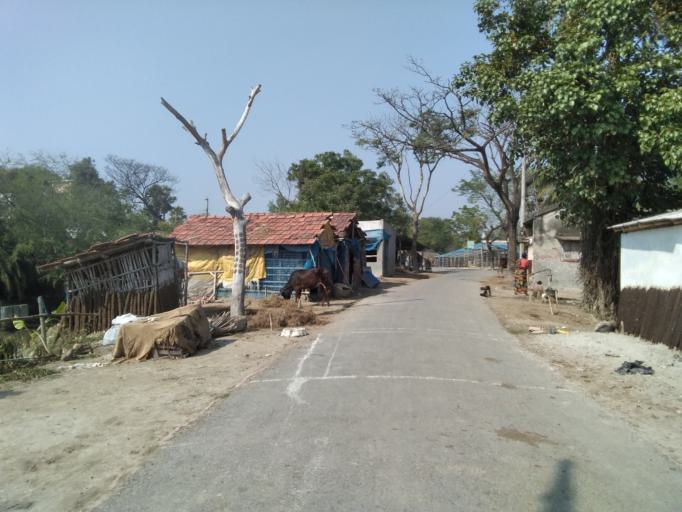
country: IN
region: West Bengal
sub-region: North 24 Parganas
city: Taki
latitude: 22.6376
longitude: 89.0009
